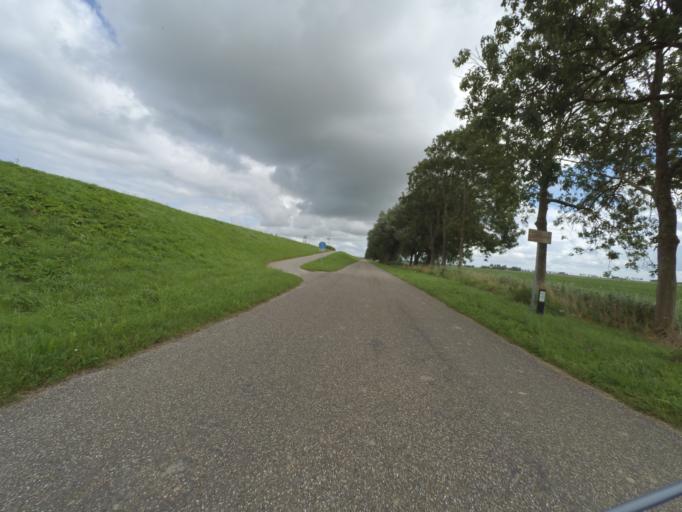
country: NL
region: Groningen
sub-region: Gemeente Zuidhorn
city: Grijpskerk
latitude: 53.3136
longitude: 6.2632
